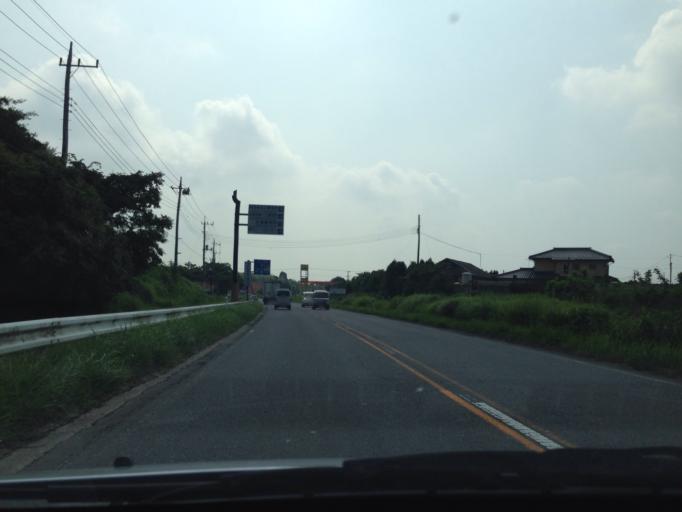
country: JP
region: Ibaraki
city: Ami
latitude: 36.0223
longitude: 140.2413
